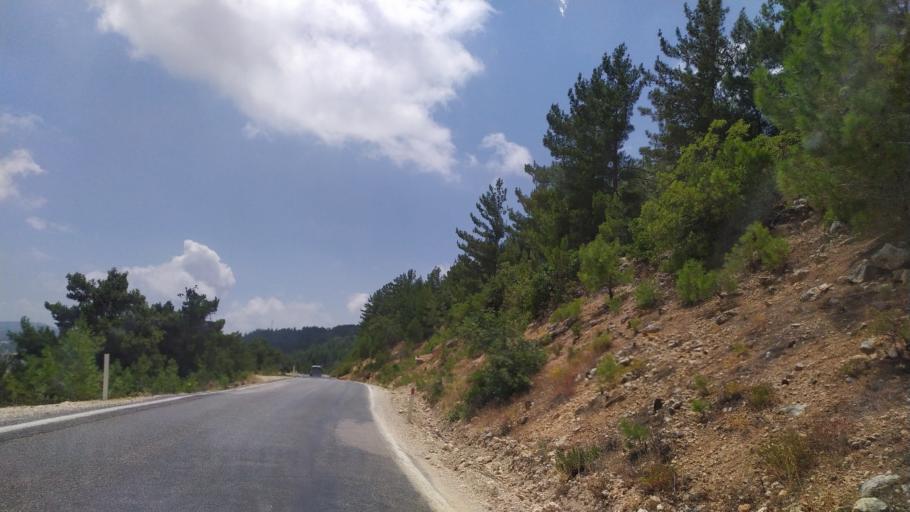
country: TR
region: Mersin
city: Gulnar
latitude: 36.3021
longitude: 33.3807
